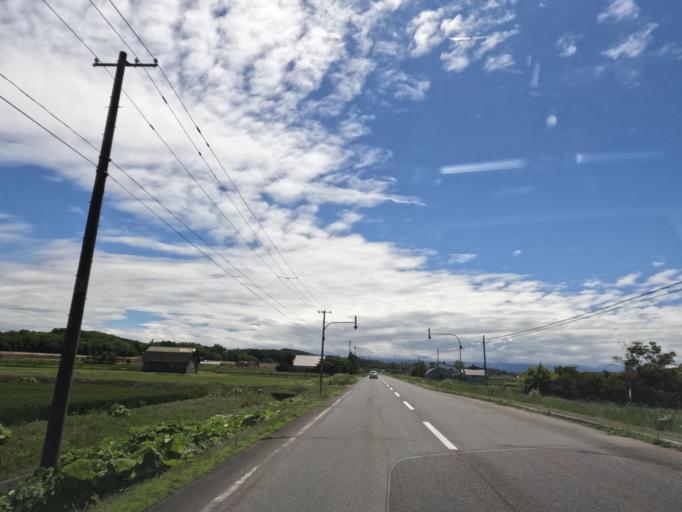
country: JP
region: Hokkaido
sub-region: Asahikawa-shi
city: Asahikawa
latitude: 43.6546
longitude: 142.4407
